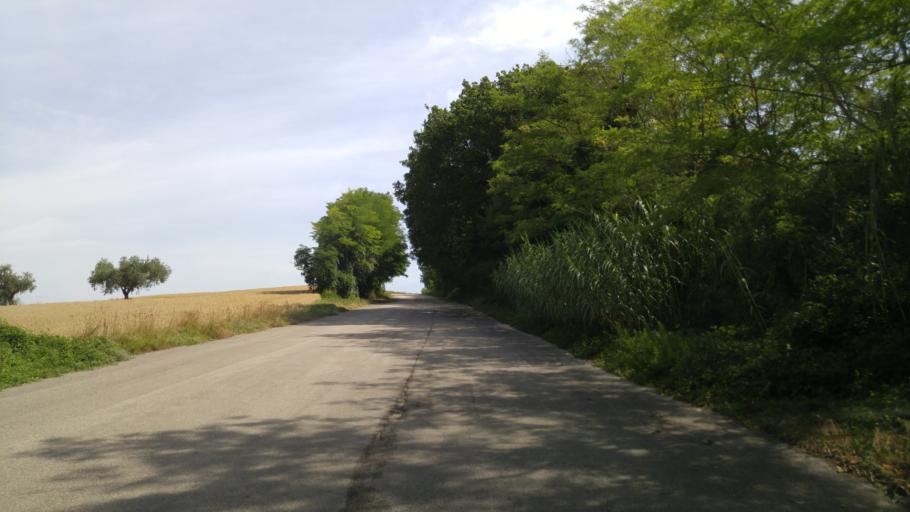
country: IT
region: The Marches
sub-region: Provincia di Pesaro e Urbino
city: Fenile
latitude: 43.8441
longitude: 12.9758
